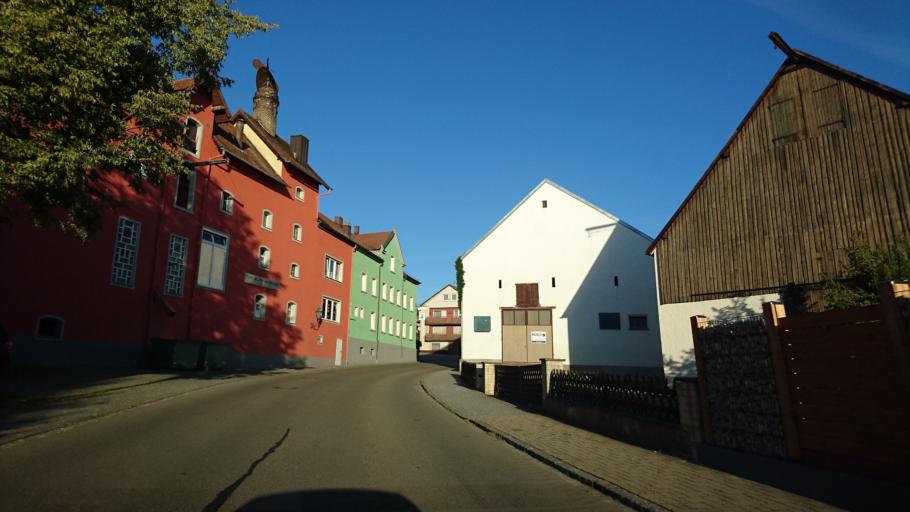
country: DE
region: Bavaria
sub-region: Regierungsbezirk Mittelfranken
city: Nennslingen
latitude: 49.0473
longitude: 11.1331
